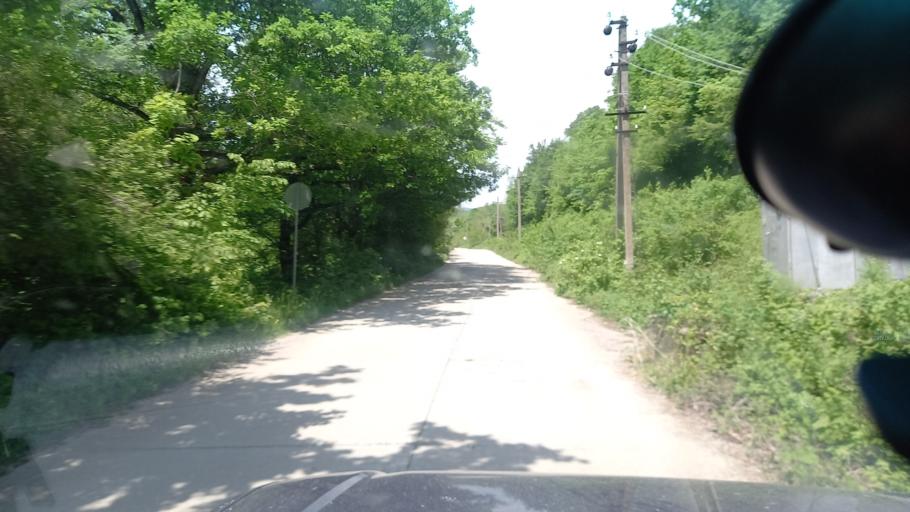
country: RU
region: Krasnodarskiy
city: Tuapse
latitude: 44.2452
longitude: 39.2397
